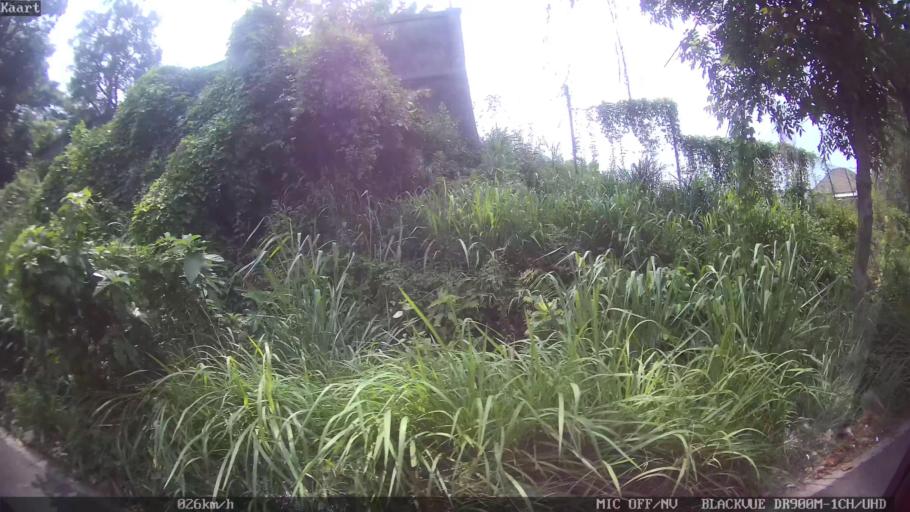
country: ID
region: Lampung
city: Bandarlampung
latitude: -5.4272
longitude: 105.2458
